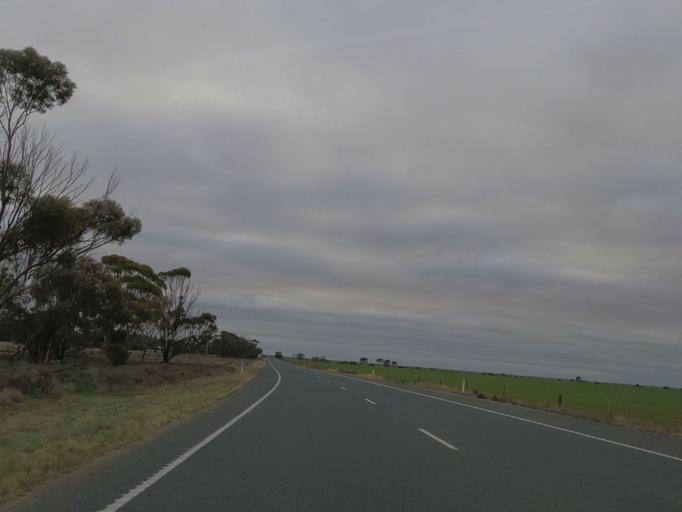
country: AU
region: Victoria
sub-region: Swan Hill
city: Swan Hill
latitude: -35.5621
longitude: 143.7823
